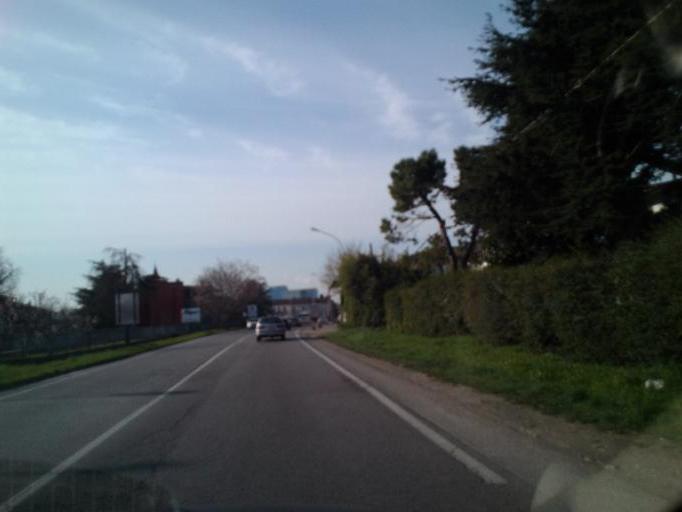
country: IT
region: Veneto
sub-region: Provincia di Verona
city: Mozzecane
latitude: 45.3224
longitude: 10.8308
